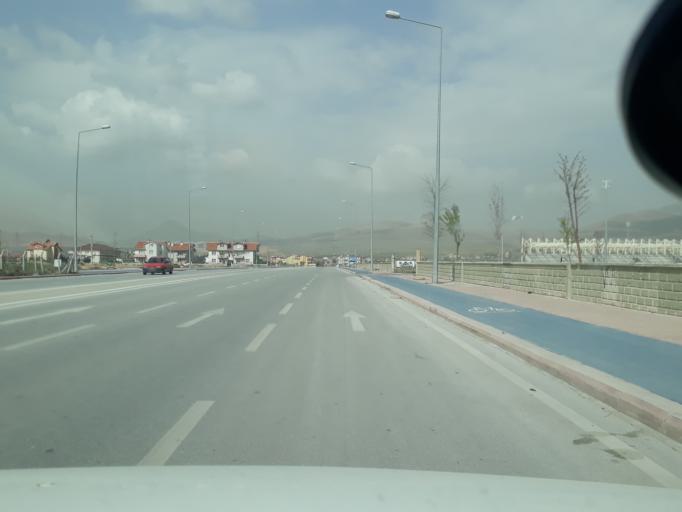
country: TR
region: Konya
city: Selcuklu
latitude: 37.9425
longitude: 32.4871
